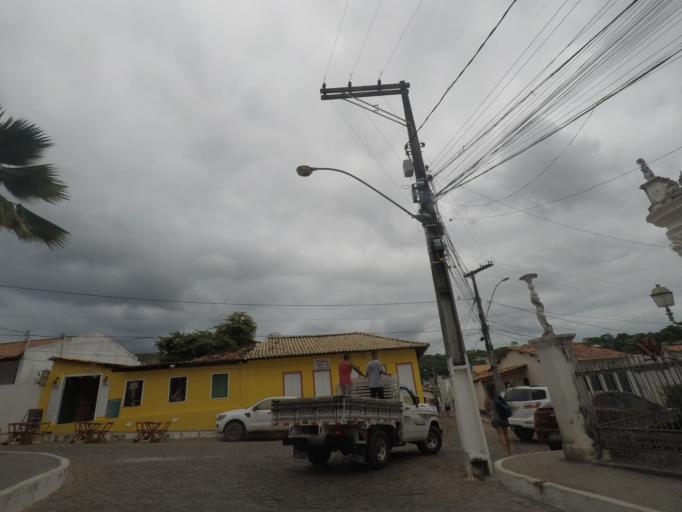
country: BR
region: Bahia
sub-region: Andarai
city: Vera Cruz
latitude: -12.5631
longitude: -41.3910
